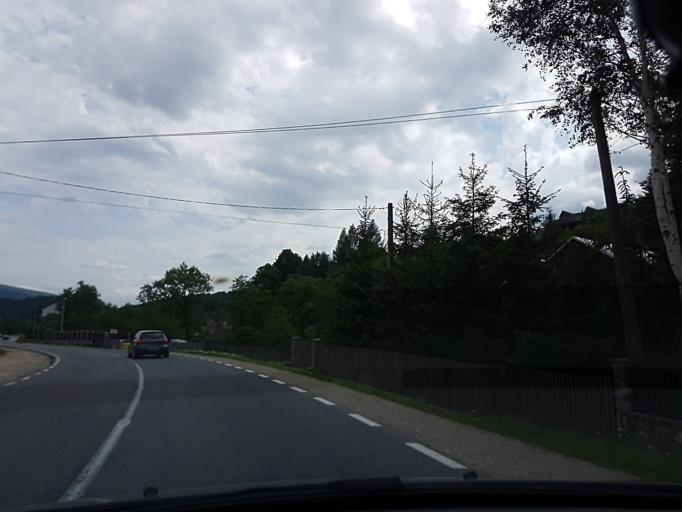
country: RO
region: Brasov
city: Crivina
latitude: 45.4527
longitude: 25.9361
